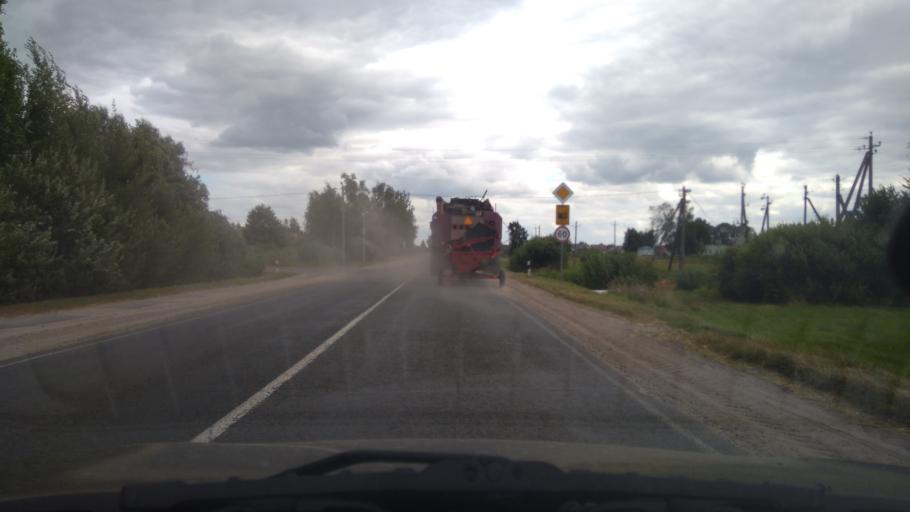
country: BY
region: Brest
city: Byelaazyorsk
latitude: 52.4928
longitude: 25.1921
